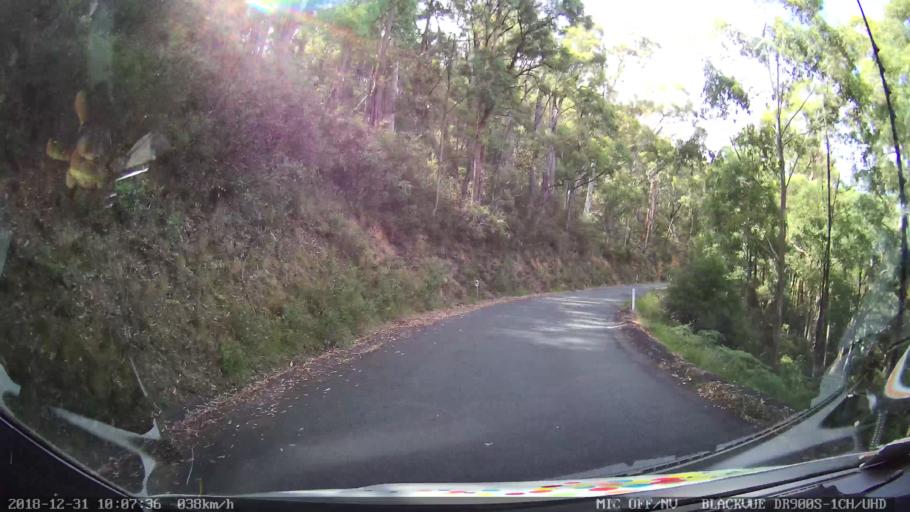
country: AU
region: New South Wales
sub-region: Snowy River
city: Jindabyne
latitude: -36.5320
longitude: 148.1831
